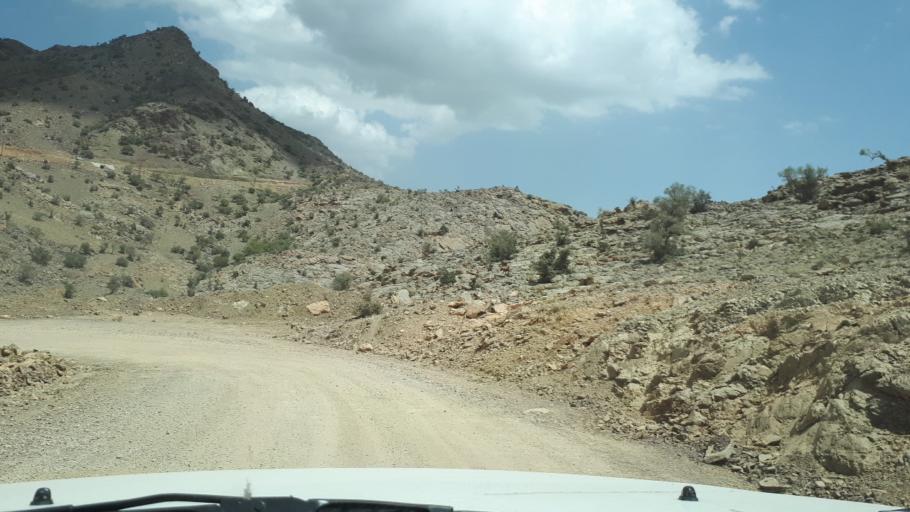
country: OM
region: Al Batinah
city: Rustaq
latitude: 23.2358
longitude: 57.1932
